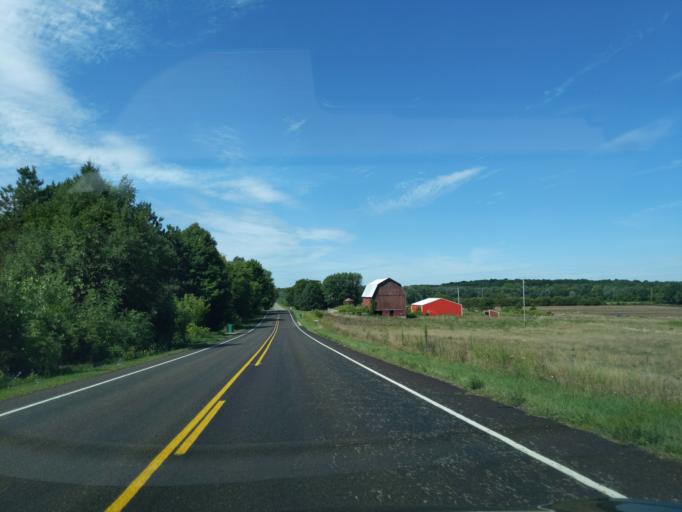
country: US
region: Michigan
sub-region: Eaton County
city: Charlotte
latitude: 42.6264
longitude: -84.9503
